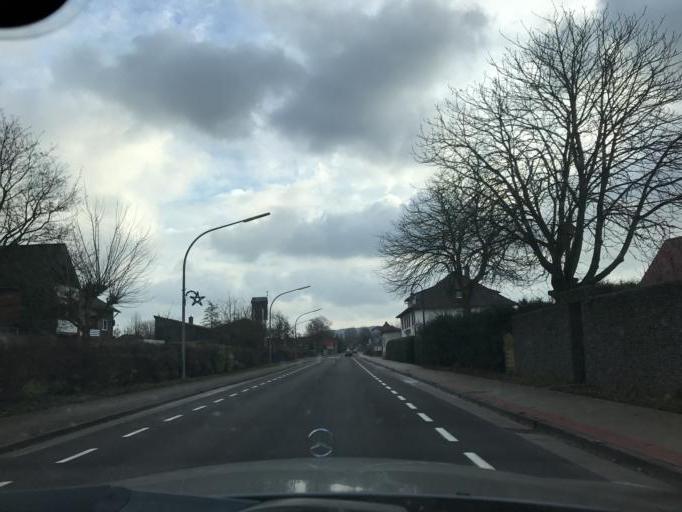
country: DE
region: Lower Saxony
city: Hasbergen
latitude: 52.2058
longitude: 7.9265
